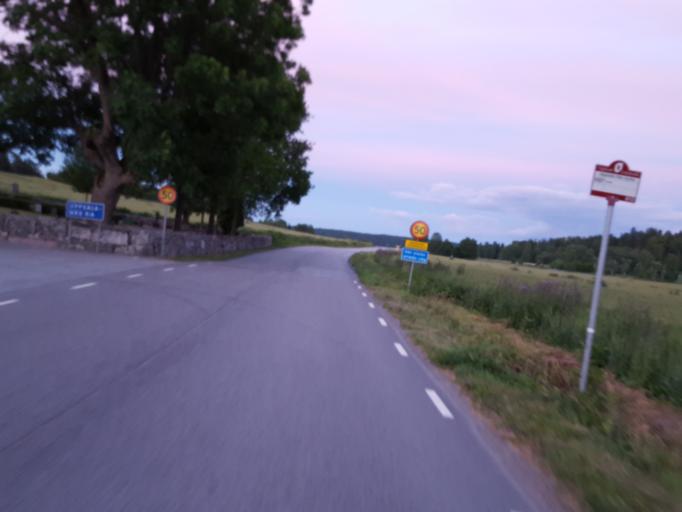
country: SE
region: Uppsala
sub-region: Uppsala Kommun
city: Uppsala
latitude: 59.7873
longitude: 17.5934
